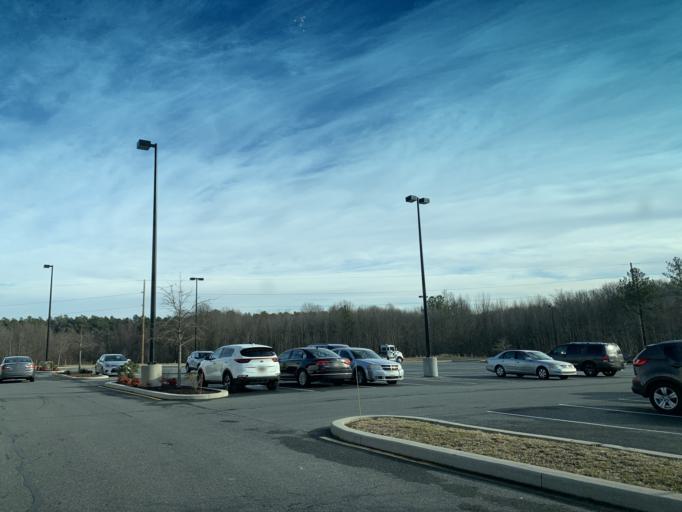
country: US
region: Delaware
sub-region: New Castle County
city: Bear
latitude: 39.6698
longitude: -75.6484
